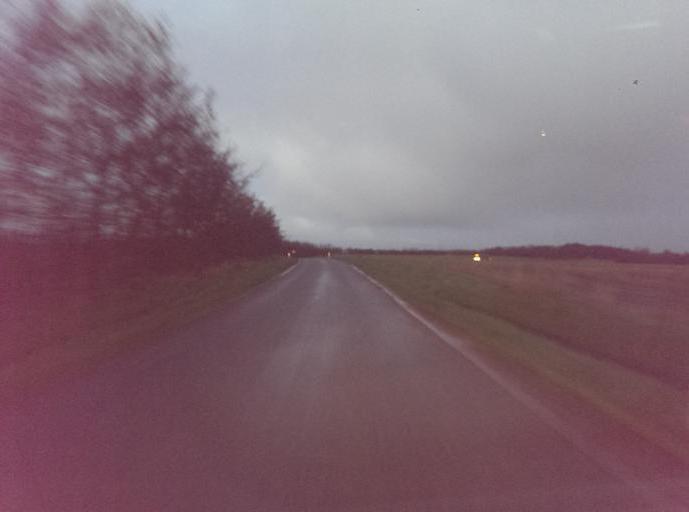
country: DK
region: South Denmark
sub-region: Esbjerg Kommune
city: Bramming
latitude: 55.4463
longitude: 8.6476
